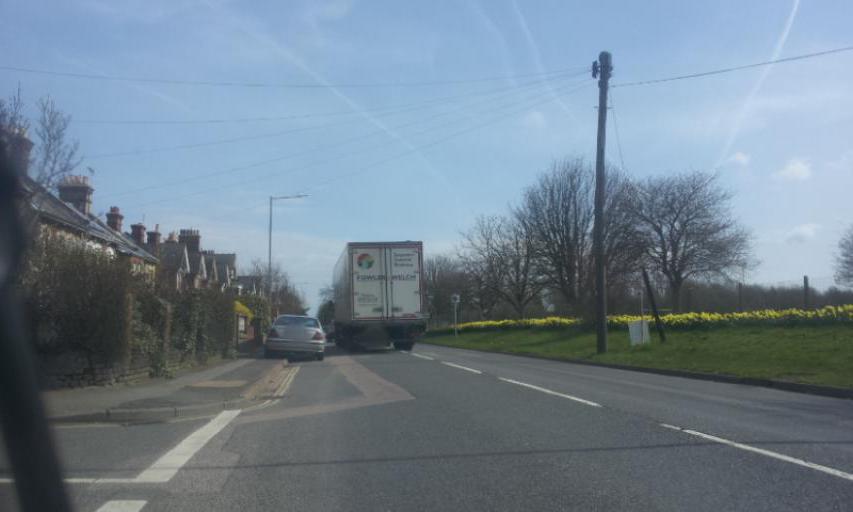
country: GB
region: England
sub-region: Kent
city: Faversham
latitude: 51.3092
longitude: 0.8855
